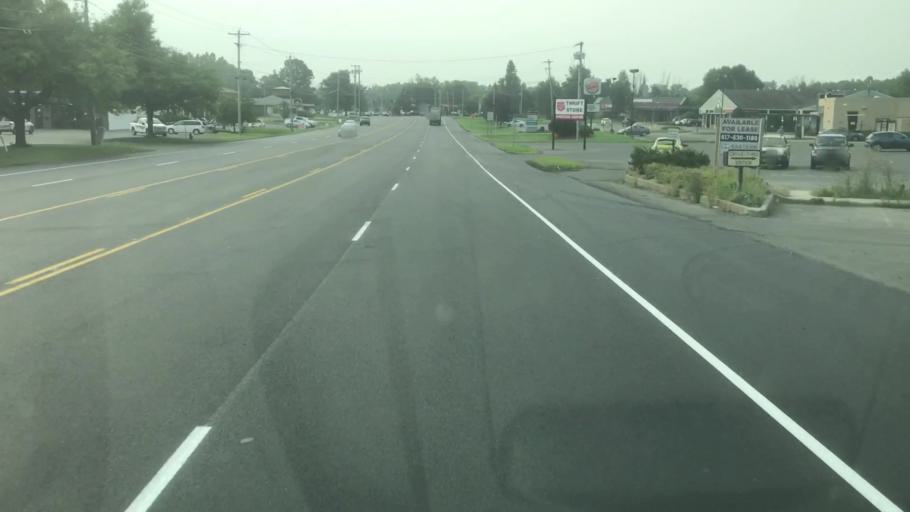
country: US
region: New York
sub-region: Onondaga County
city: Liverpool
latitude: 43.1388
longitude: -76.2269
